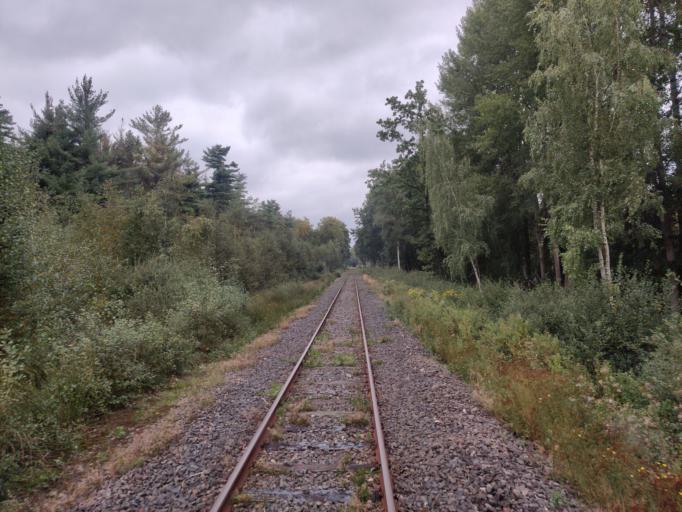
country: DE
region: Lower Saxony
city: Gnarrenburg
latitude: 53.4017
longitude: 9.0120
